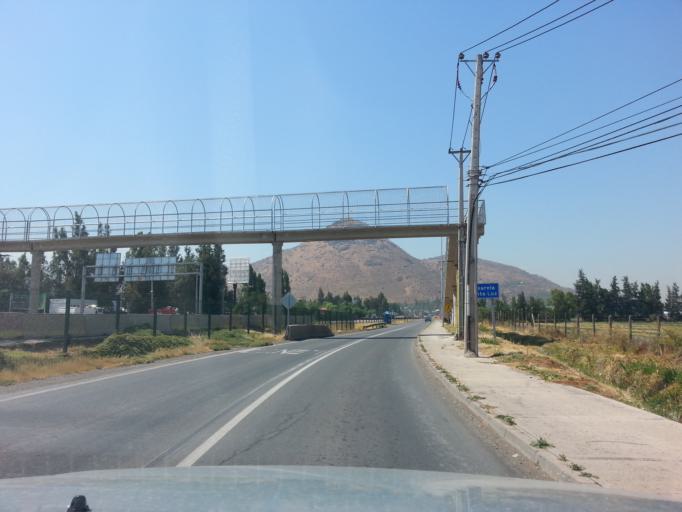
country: CL
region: Santiago Metropolitan
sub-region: Provincia de Chacabuco
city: Chicureo Abajo
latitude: -33.2936
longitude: -70.7021
